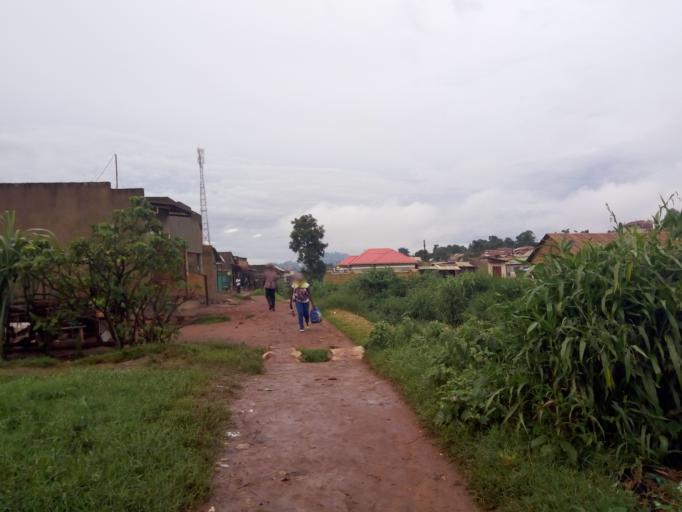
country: UG
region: Central Region
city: Kampala Central Division
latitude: 0.3405
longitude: 32.5584
